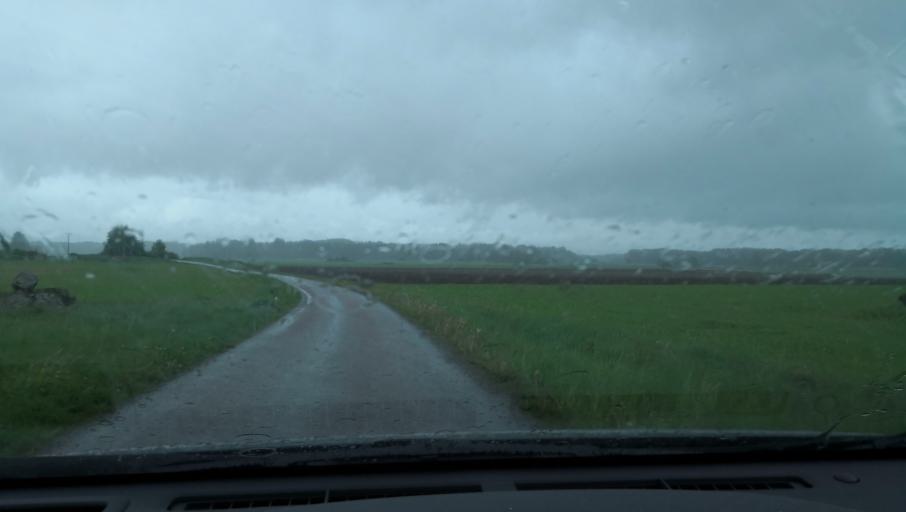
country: SE
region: Uppsala
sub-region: Enkopings Kommun
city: Orsundsbro
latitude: 59.7747
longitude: 17.3485
